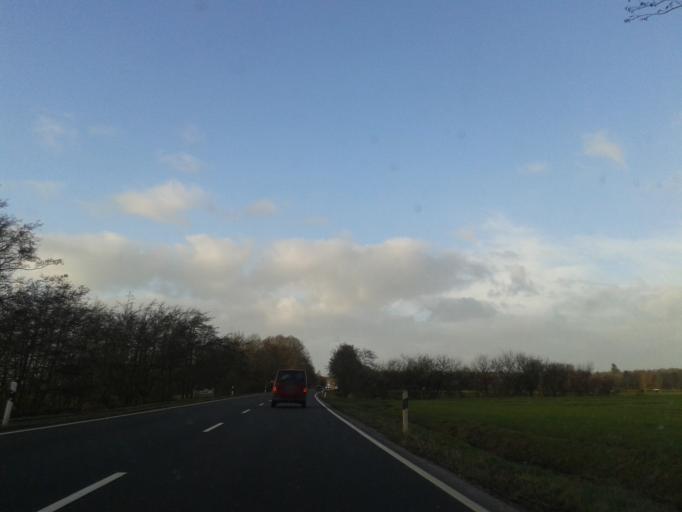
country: DE
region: Lower Saxony
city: Osteel
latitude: 53.5613
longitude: 7.2489
